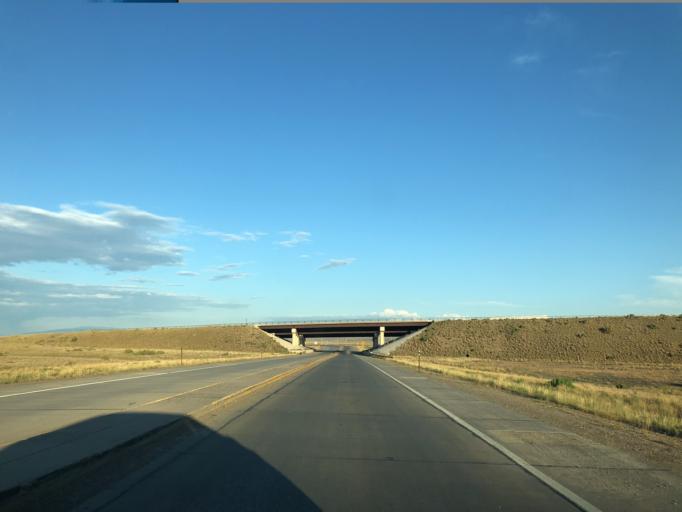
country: US
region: Wyoming
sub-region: Carbon County
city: Rawlins
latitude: 41.7904
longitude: -107.2025
